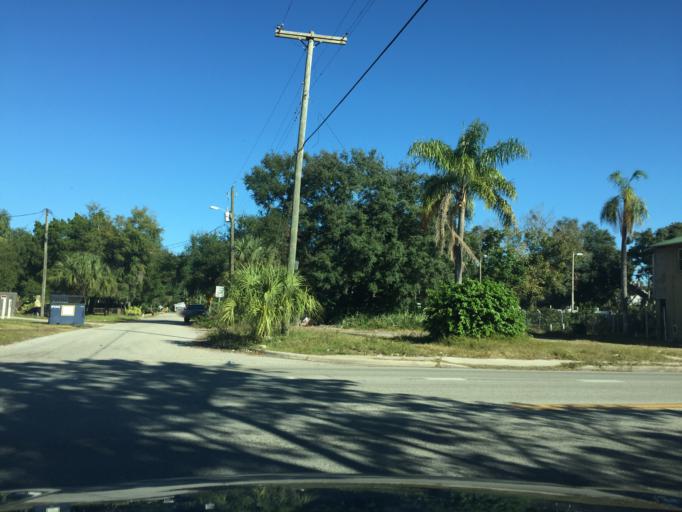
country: US
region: Florida
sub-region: Hillsborough County
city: Tampa
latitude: 27.9707
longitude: -82.4521
